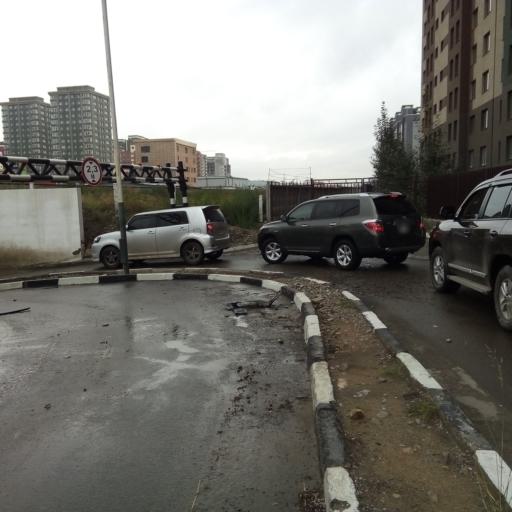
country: MN
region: Ulaanbaatar
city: Ulaanbaatar
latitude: 47.9072
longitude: 106.9358
